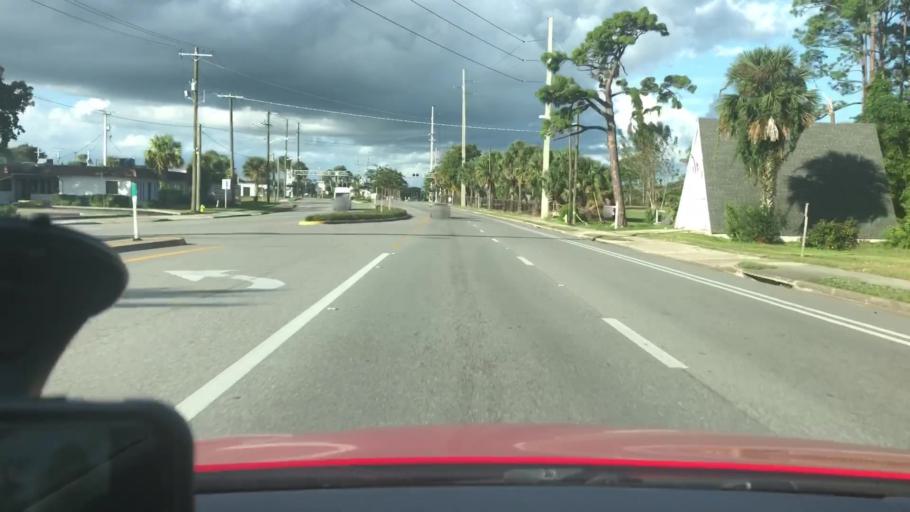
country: US
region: Florida
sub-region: Volusia County
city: South Daytona
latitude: 29.1834
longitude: -81.0096
